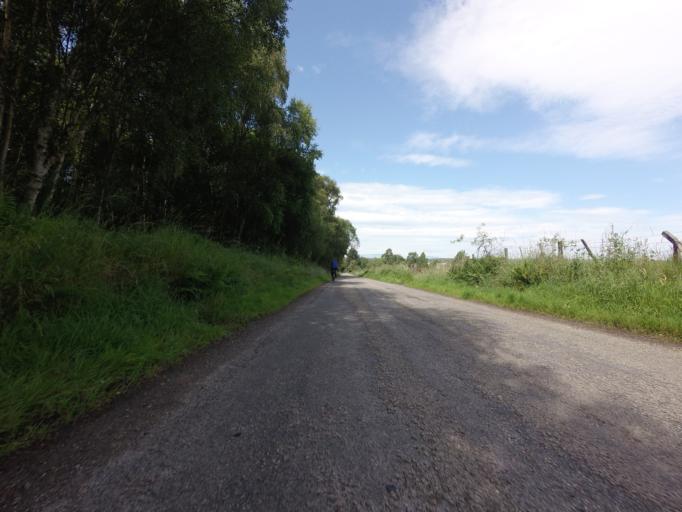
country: GB
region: Scotland
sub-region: Highland
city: Inverness
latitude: 57.5195
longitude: -4.2941
